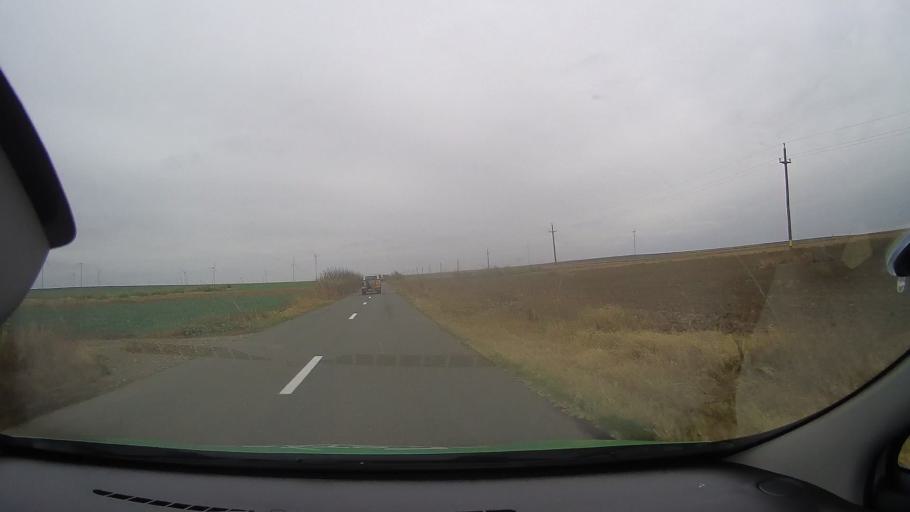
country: RO
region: Constanta
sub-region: Comuna Targusor
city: Targusor
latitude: 44.4682
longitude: 28.3913
